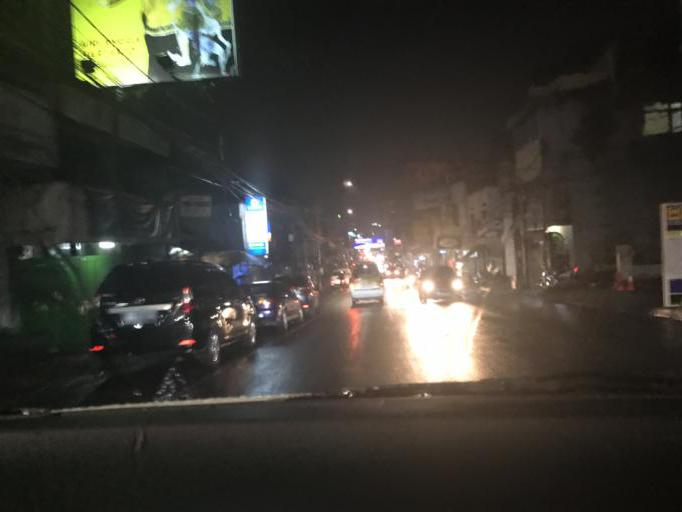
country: ID
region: West Java
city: Bandung
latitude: -6.8911
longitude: 107.5970
